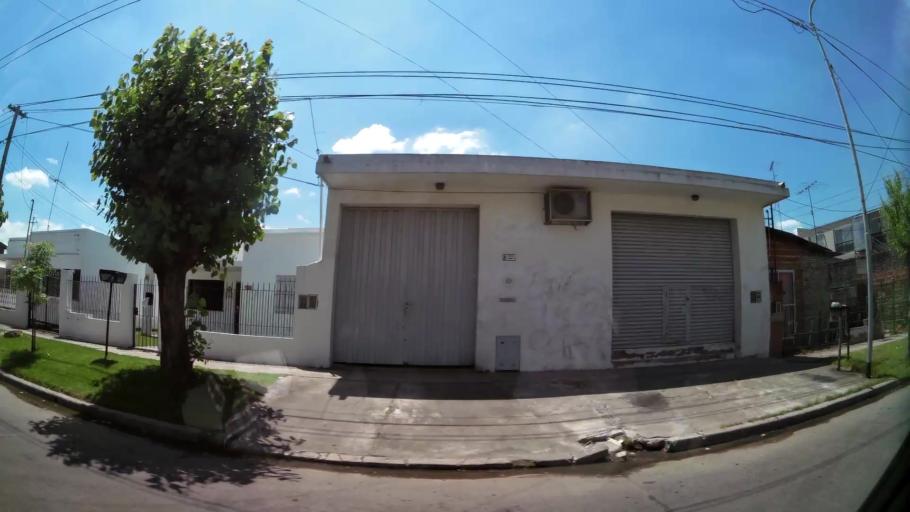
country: AR
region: Buenos Aires
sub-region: Partido de Tigre
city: Tigre
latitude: -34.4402
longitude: -58.5807
